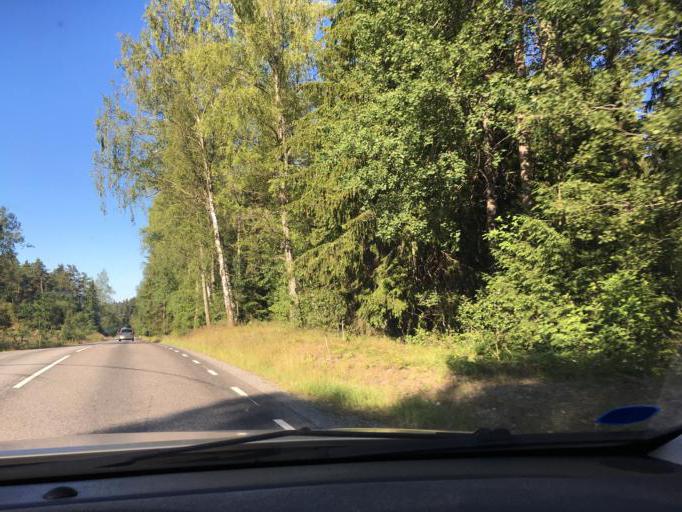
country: SE
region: Stockholm
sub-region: Salems Kommun
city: Ronninge
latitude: 59.2289
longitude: 17.6883
